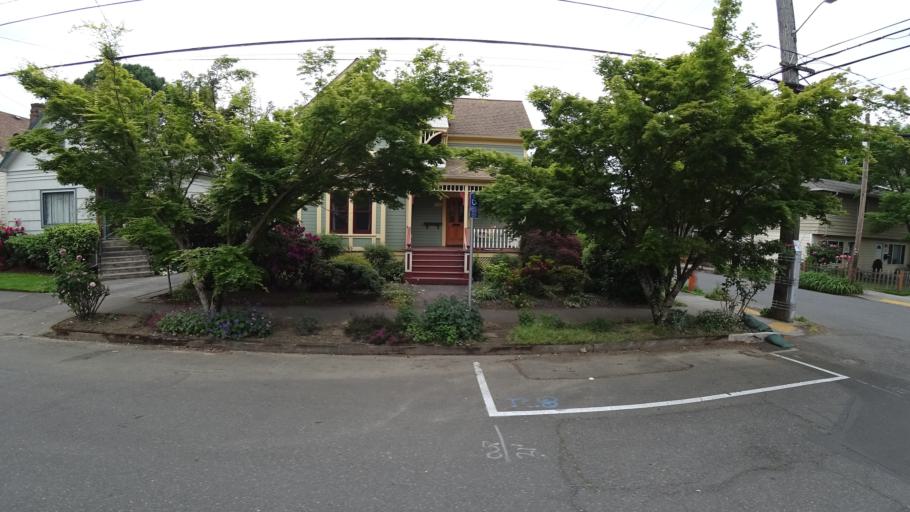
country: US
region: Oregon
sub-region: Multnomah County
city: Lents
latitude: 45.5136
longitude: -122.6160
